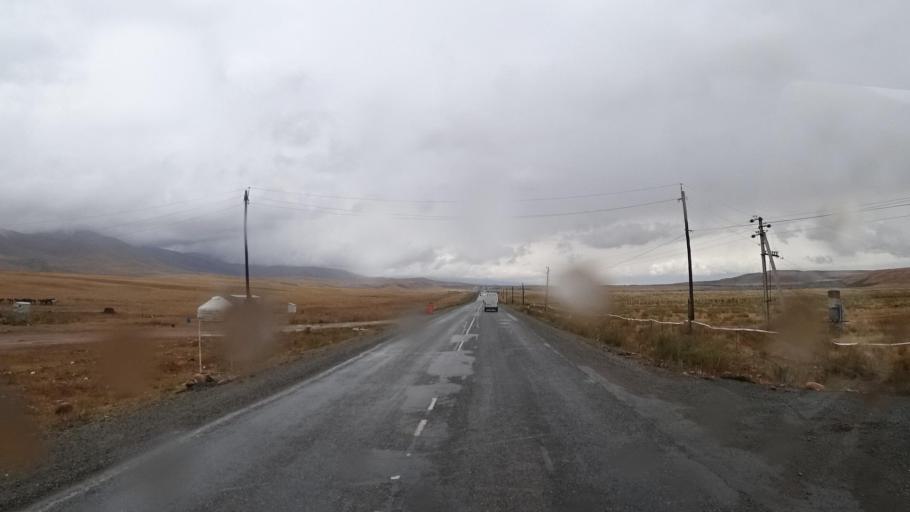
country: KG
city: Sosnovka
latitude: 42.2205
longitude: 73.6992
